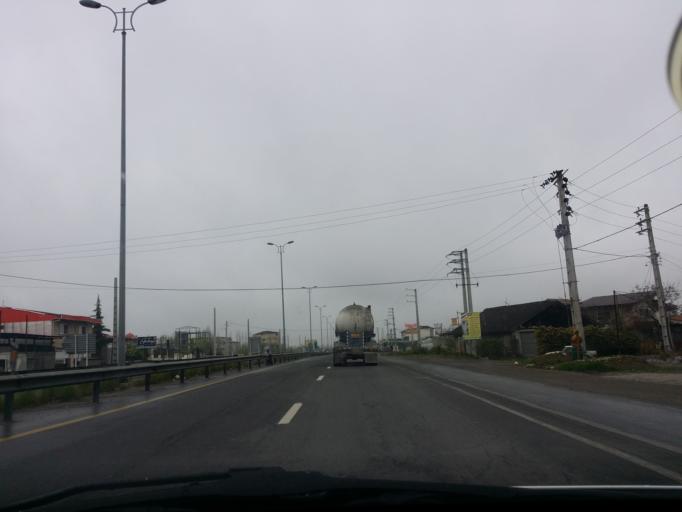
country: IR
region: Mazandaran
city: Tonekabon
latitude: 36.7960
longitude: 50.9100
